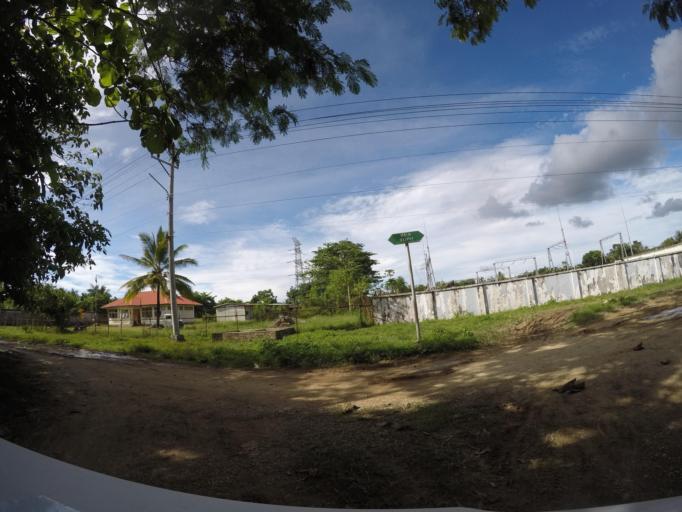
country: TL
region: Lautem
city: Lospalos
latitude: -8.4922
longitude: 126.9944
